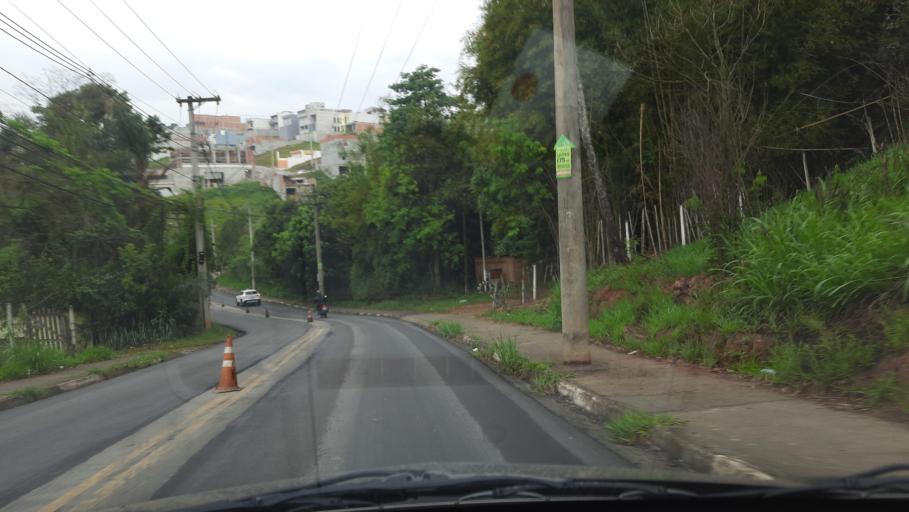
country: BR
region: Sao Paulo
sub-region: Caieiras
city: Caieiras
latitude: -23.3783
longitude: -46.7013
